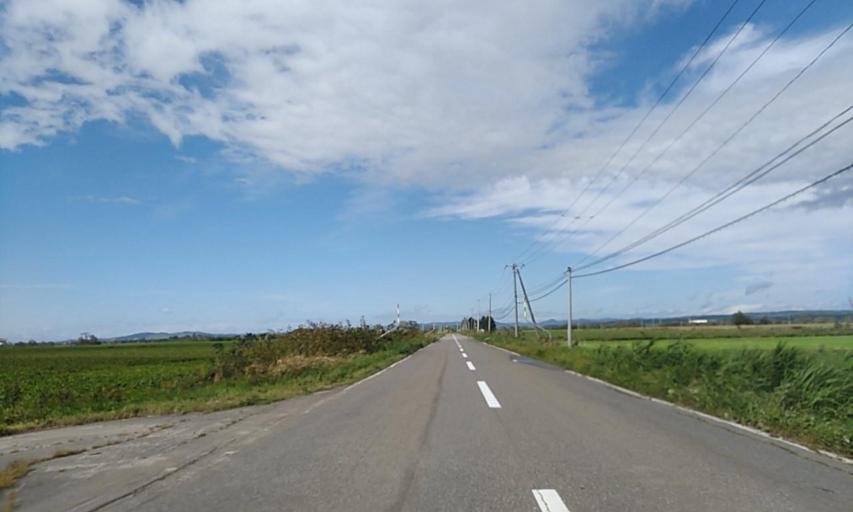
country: JP
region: Hokkaido
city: Obihiro
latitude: 42.7245
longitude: 143.6331
